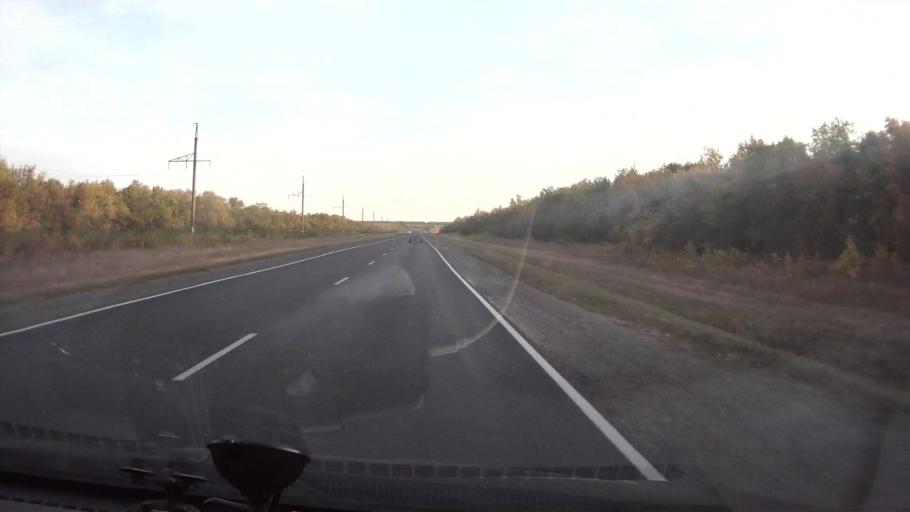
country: RU
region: Saratov
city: Krasnoarmeysk
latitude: 51.1163
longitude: 45.6506
